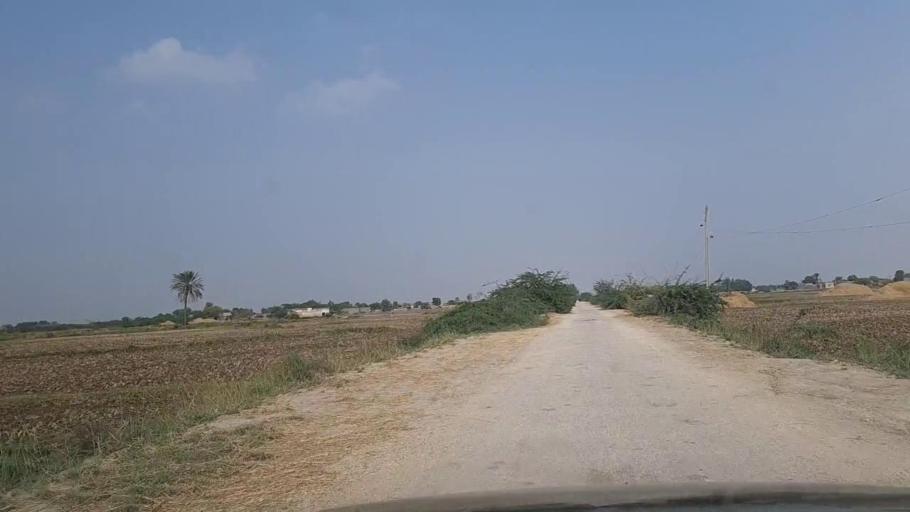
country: PK
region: Sindh
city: Thatta
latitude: 24.7931
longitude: 67.8735
